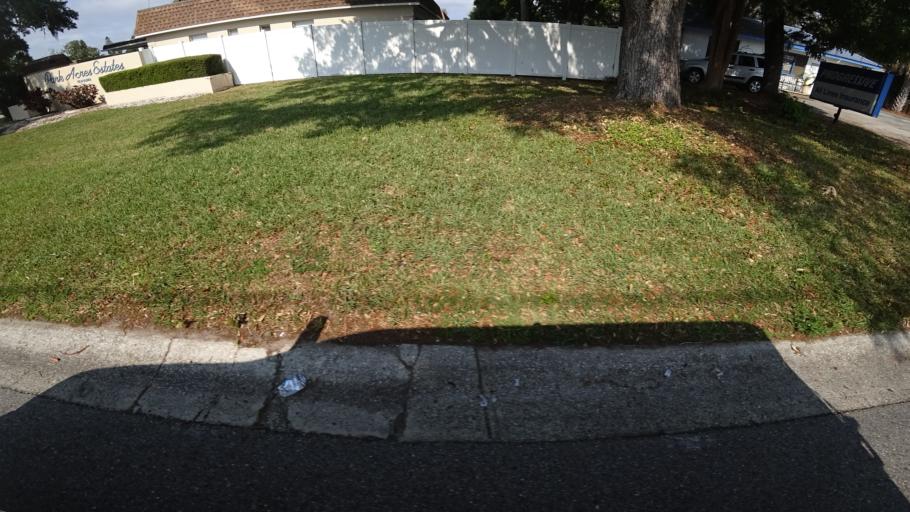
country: US
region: Florida
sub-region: Manatee County
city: South Bradenton
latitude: 27.4573
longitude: -82.5671
